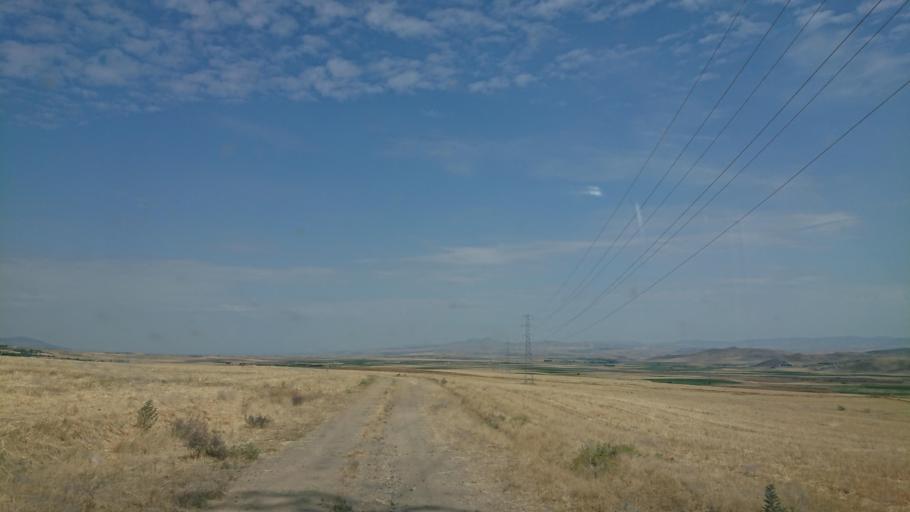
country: TR
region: Aksaray
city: Agacoren
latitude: 38.9508
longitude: 33.9114
